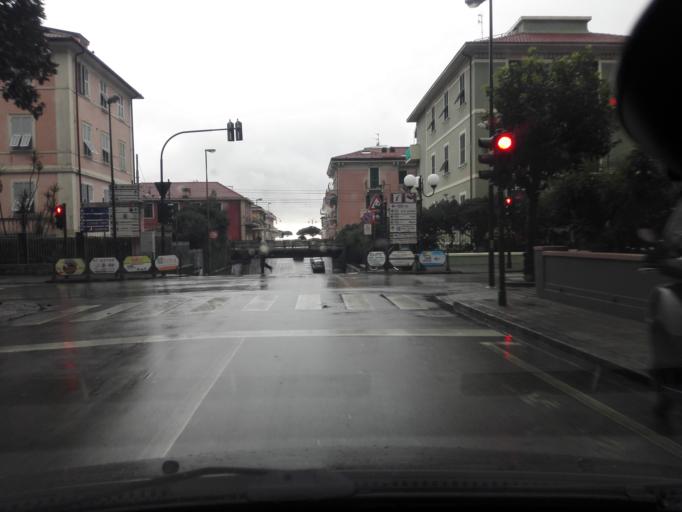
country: IT
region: Liguria
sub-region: Provincia di Genova
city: Chiavari
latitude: 44.3178
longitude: 9.3179
